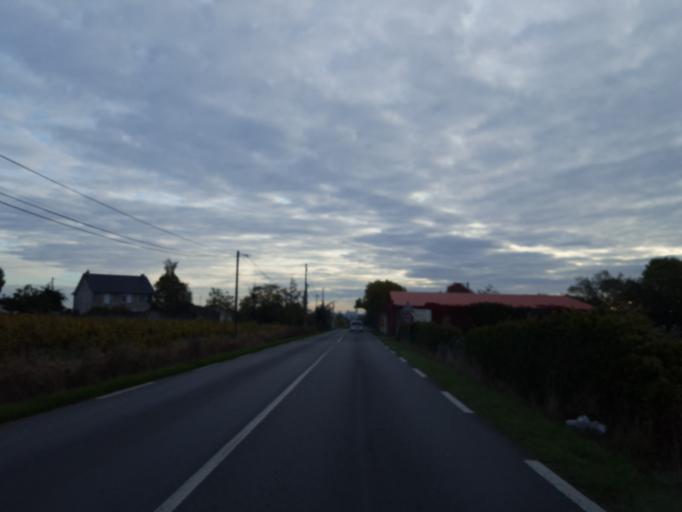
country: FR
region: Pays de la Loire
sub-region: Departement de la Loire-Atlantique
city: Saint-Julien-de-Concelles
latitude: 47.2347
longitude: -1.3875
